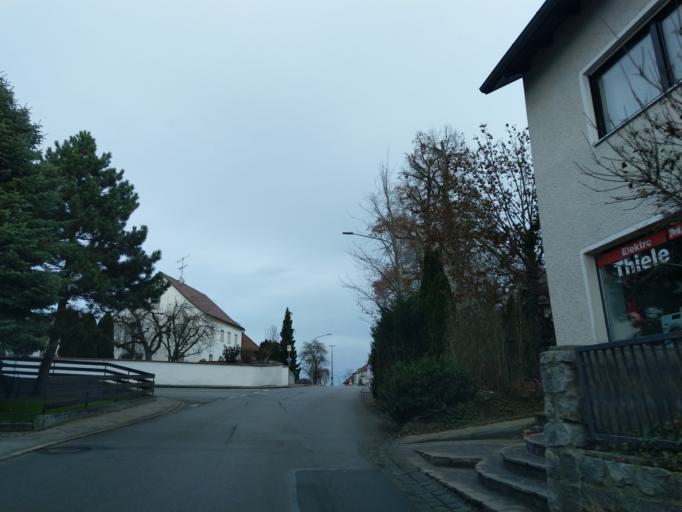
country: DE
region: Bavaria
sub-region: Lower Bavaria
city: Osterhofen
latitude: 48.6915
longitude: 13.0132
